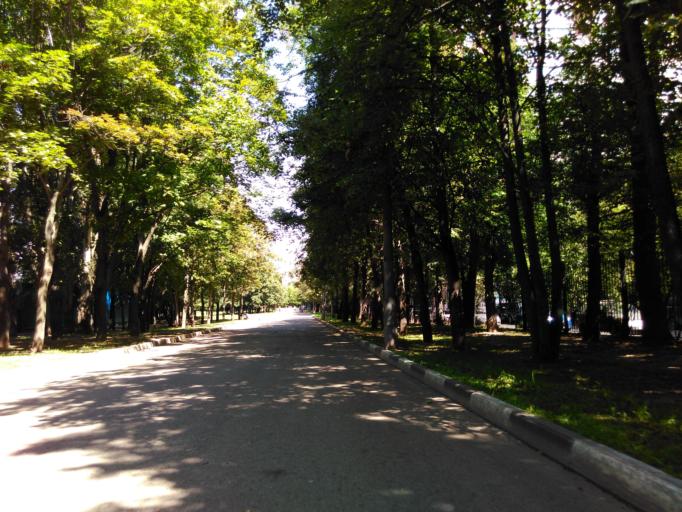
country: RU
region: Moskovskaya
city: Leninskiye Gory
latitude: 55.7019
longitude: 37.5599
